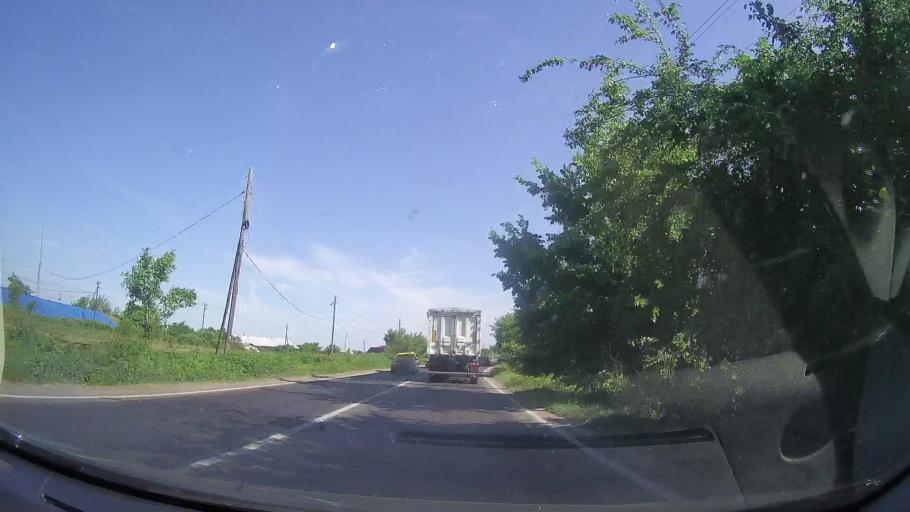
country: RO
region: Prahova
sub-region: Comuna Blejoiu
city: Ploiestiori
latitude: 44.9899
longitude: 26.0150
